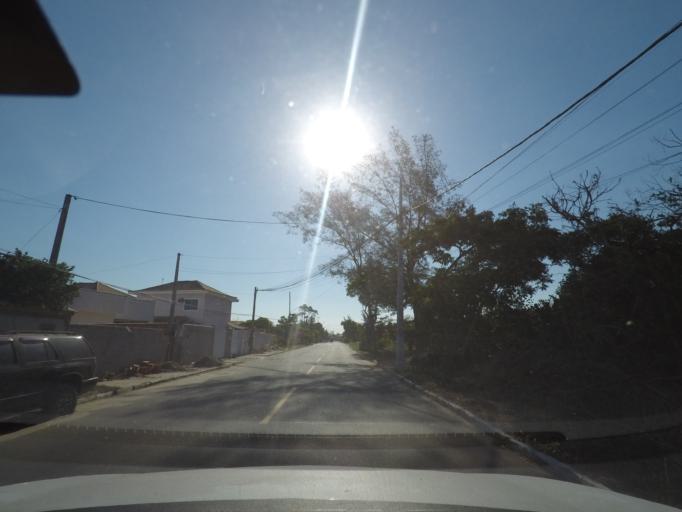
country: BR
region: Rio de Janeiro
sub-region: Marica
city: Marica
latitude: -22.9710
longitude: -42.9173
